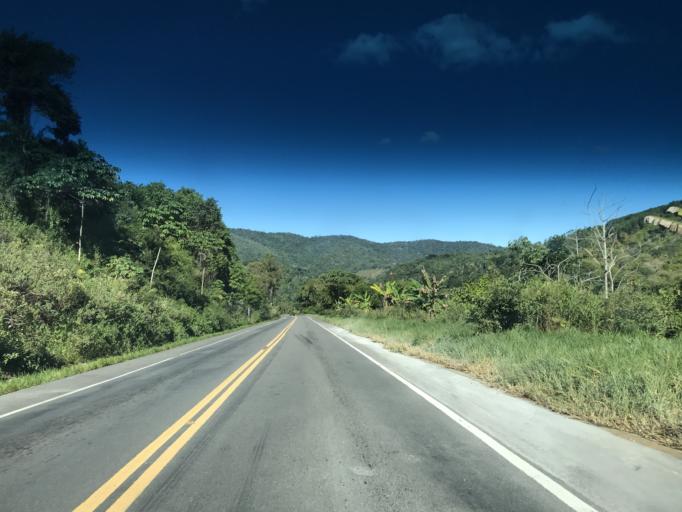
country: BR
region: Bahia
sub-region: Gandu
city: Gandu
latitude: -13.8822
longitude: -39.4883
